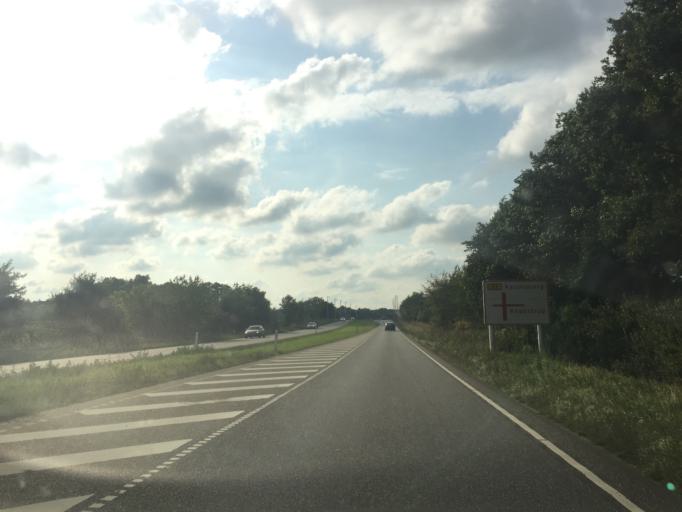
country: DK
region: Zealand
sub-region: Soro Kommune
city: Stenlille
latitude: 55.6589
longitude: 11.5704
